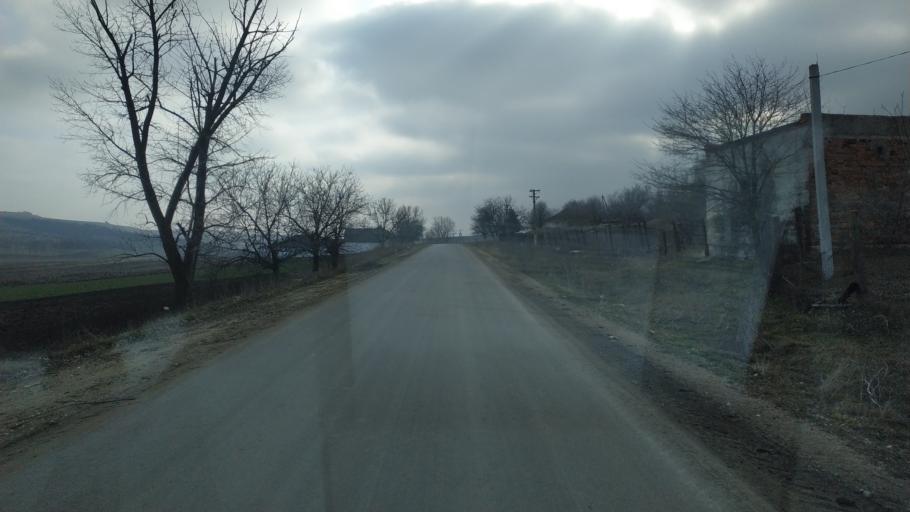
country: MD
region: Nisporeni
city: Nisporeni
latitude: 46.9322
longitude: 28.3281
